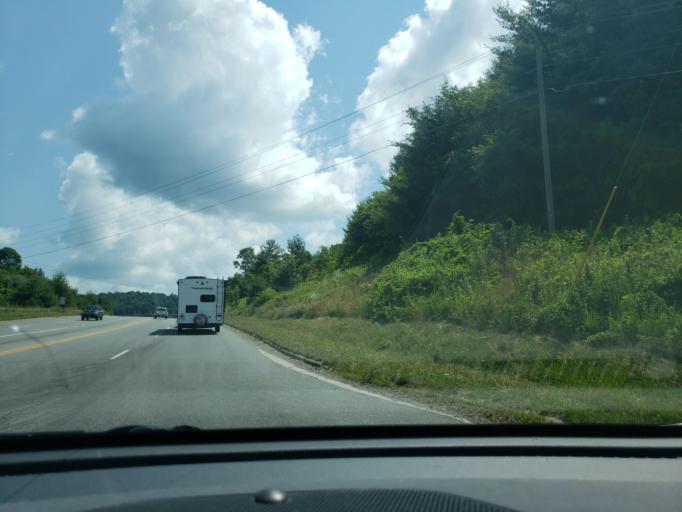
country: US
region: North Carolina
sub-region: Watauga County
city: Boone
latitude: 36.2213
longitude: -81.6387
